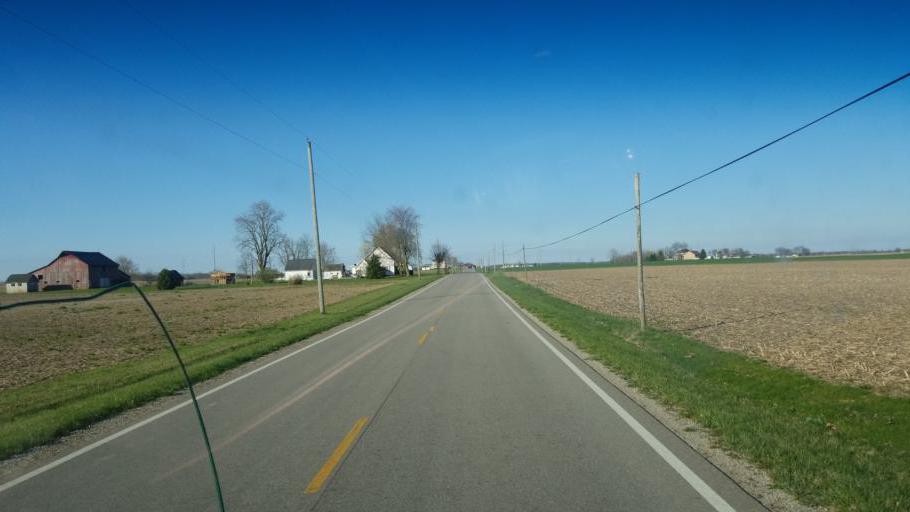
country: US
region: Ohio
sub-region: Union County
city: Richwood
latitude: 40.4457
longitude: -83.4657
